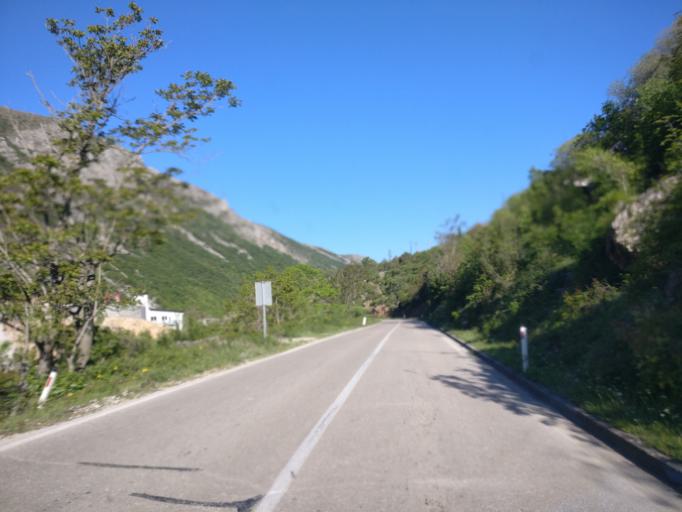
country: BA
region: Federation of Bosnia and Herzegovina
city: Stolac
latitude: 43.0781
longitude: 18.0200
